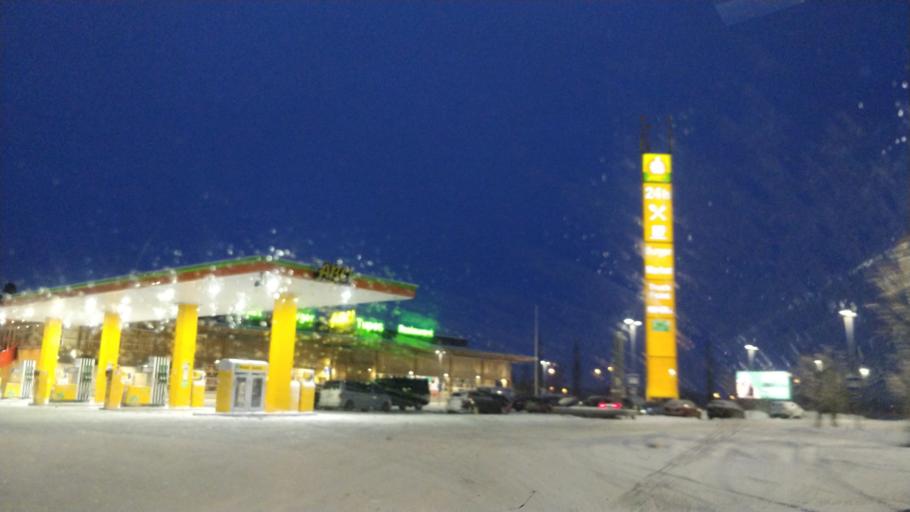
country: FI
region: Northern Ostrobothnia
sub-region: Oulu
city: Kempele
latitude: 64.8623
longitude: 25.5232
